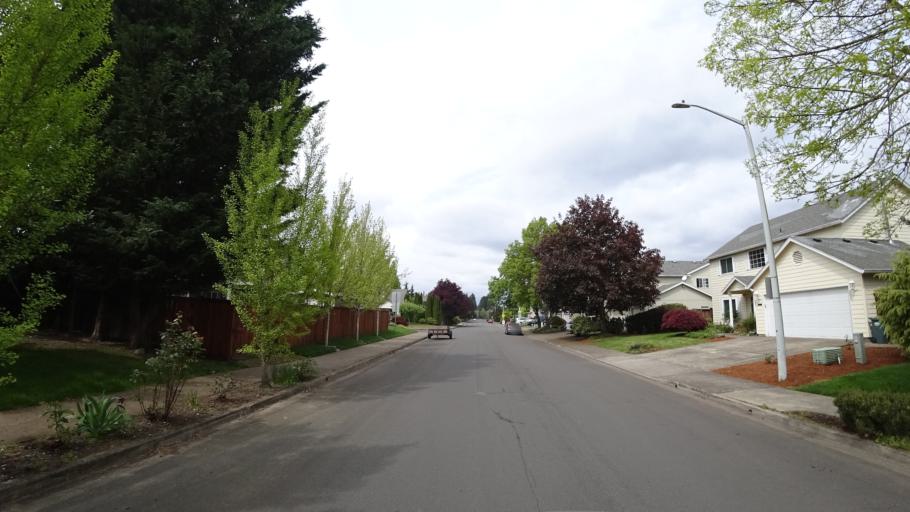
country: US
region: Oregon
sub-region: Washington County
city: Hillsboro
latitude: 45.5487
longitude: -122.9908
